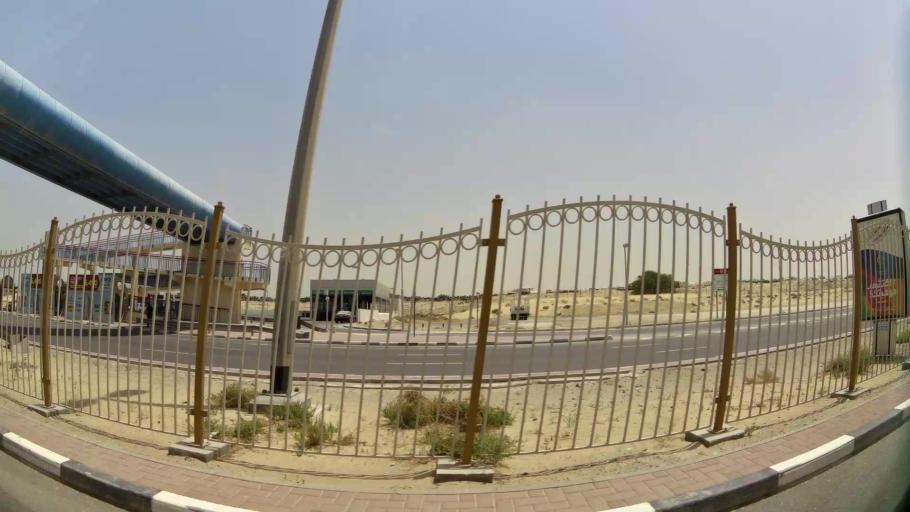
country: AE
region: Ash Shariqah
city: Sharjah
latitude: 25.2819
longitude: 55.4119
